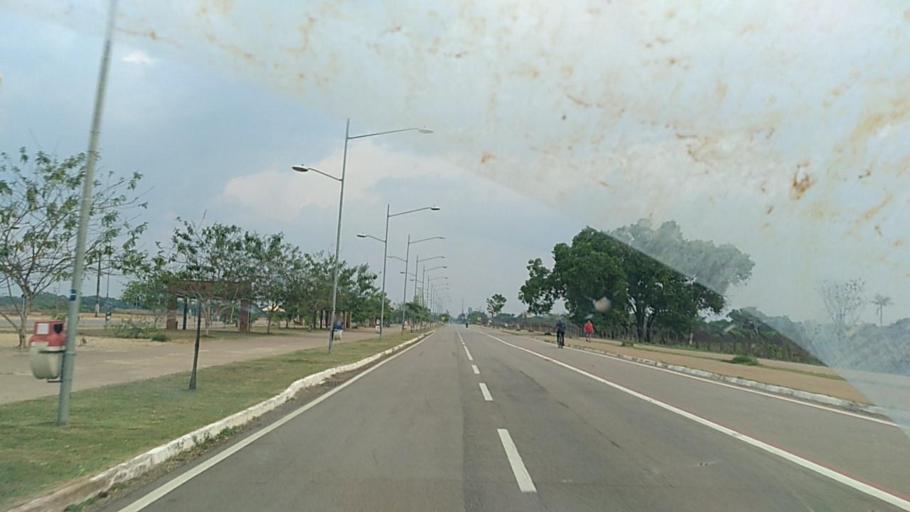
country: BR
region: Rondonia
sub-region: Porto Velho
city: Porto Velho
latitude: -8.7229
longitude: -63.8939
